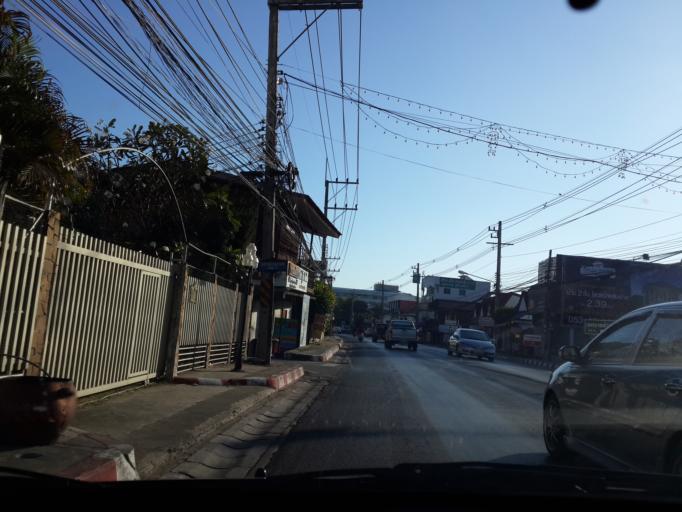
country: TH
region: Chiang Mai
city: Hang Dong
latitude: 18.6864
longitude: 98.9195
